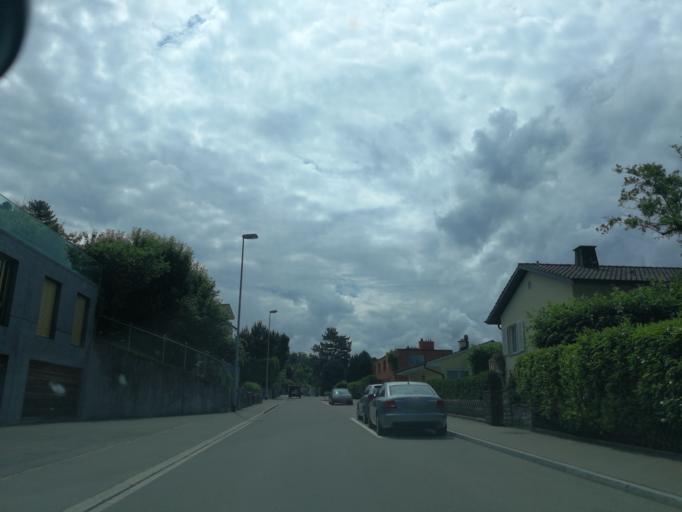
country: CH
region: Zurich
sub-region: Bezirk Meilen
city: Erlenbach / links des Dorfbachs oberhalb Bahnlinie
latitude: 47.2991
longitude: 8.6022
